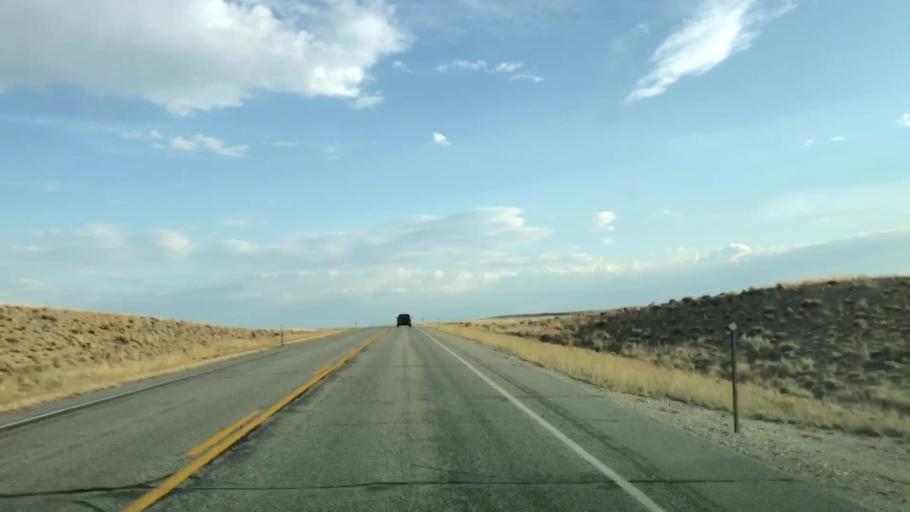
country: US
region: Wyoming
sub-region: Sublette County
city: Pinedale
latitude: 42.3447
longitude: -109.5219
